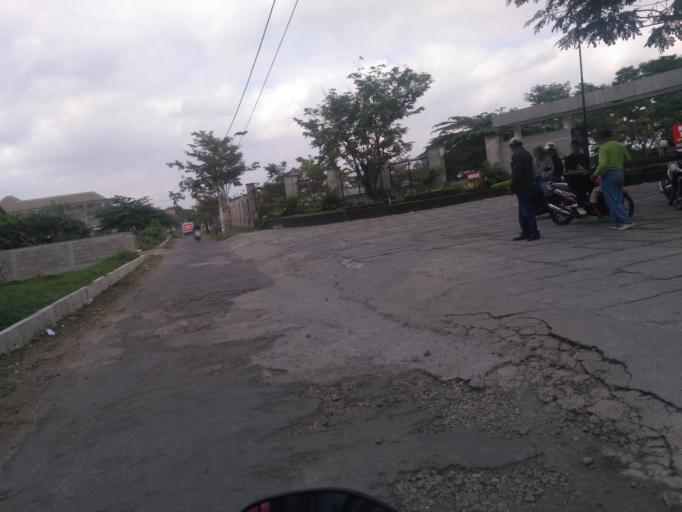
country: ID
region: Daerah Istimewa Yogyakarta
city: Melati
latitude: -7.7484
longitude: 110.3560
